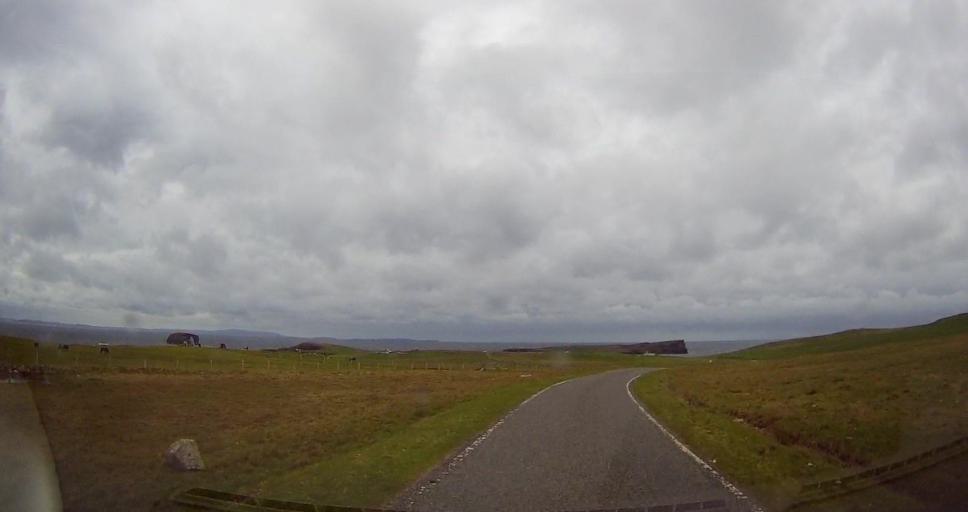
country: GB
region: Scotland
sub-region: Shetland Islands
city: Lerwick
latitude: 60.4874
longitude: -1.6016
